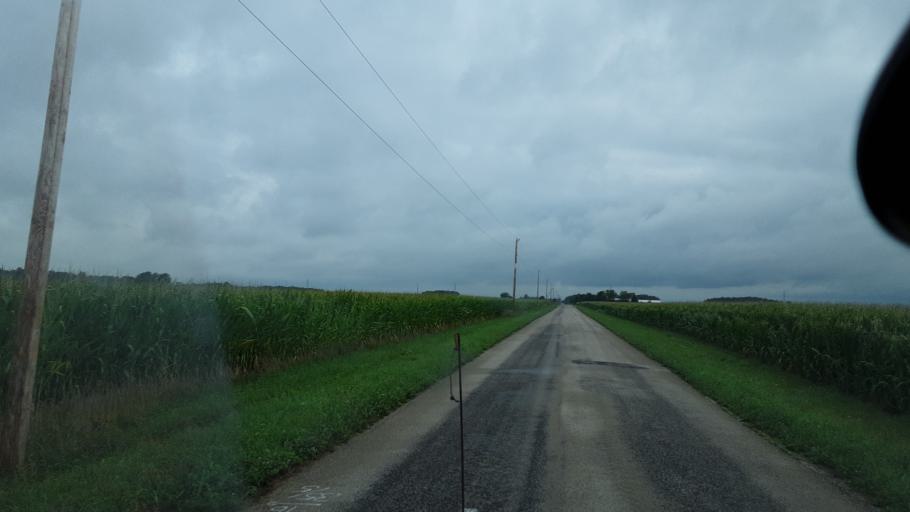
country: US
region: Indiana
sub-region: Allen County
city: Monroeville
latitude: 40.9102
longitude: -84.8426
